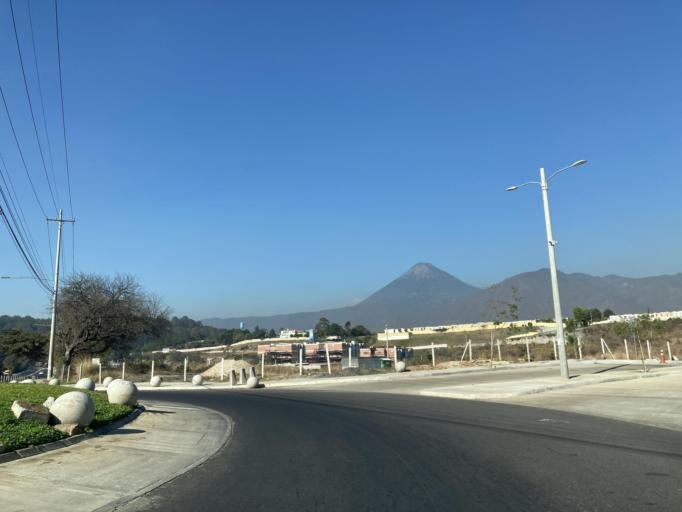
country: GT
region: Guatemala
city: Amatitlan
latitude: 14.5053
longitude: -90.6112
